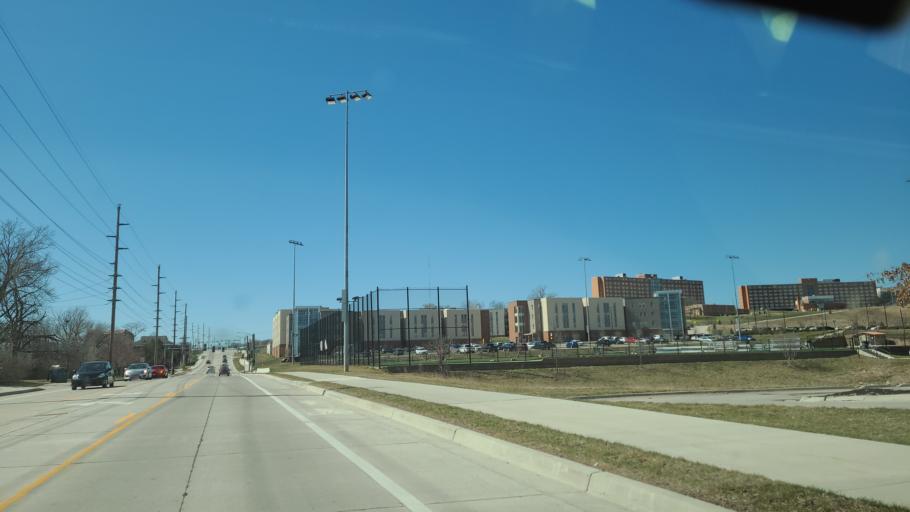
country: US
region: Kansas
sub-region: Douglas County
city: Lawrence
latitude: 38.9501
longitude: -95.2537
